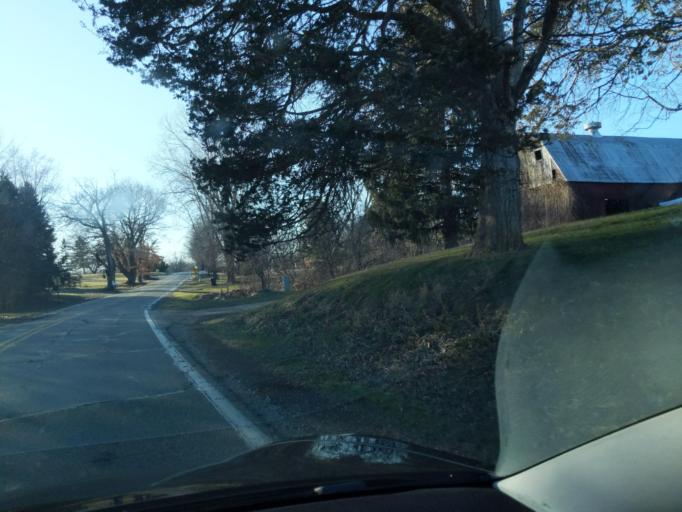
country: US
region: Michigan
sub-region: Ingham County
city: Stockbridge
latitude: 42.4467
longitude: -84.0715
